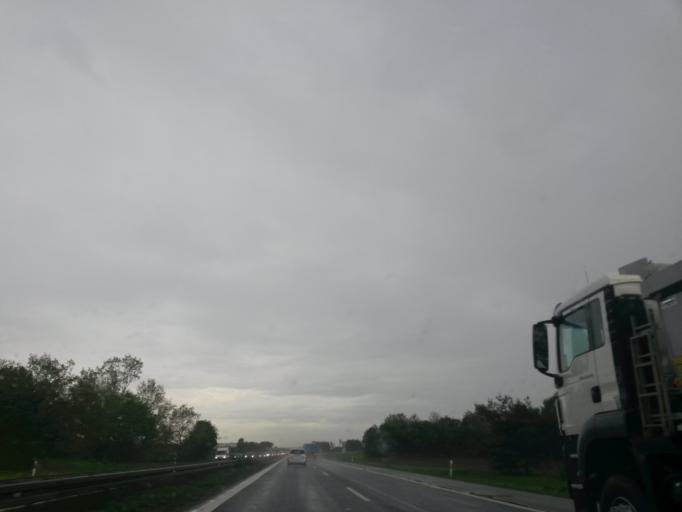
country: DE
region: Bavaria
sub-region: Upper Franconia
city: Hausen
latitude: 49.6822
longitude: 11.0539
